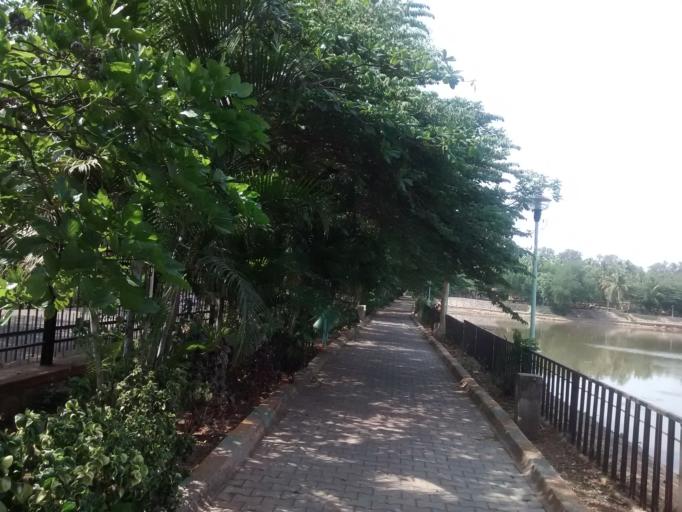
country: IN
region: Karnataka
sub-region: Dharwad
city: Hubli
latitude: 15.4635
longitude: 74.9859
